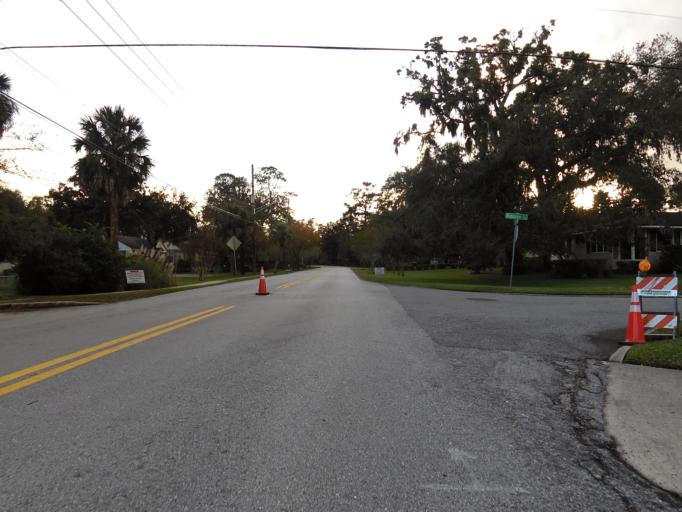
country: US
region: Florida
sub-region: Duval County
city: Jacksonville
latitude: 30.2877
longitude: -81.6550
